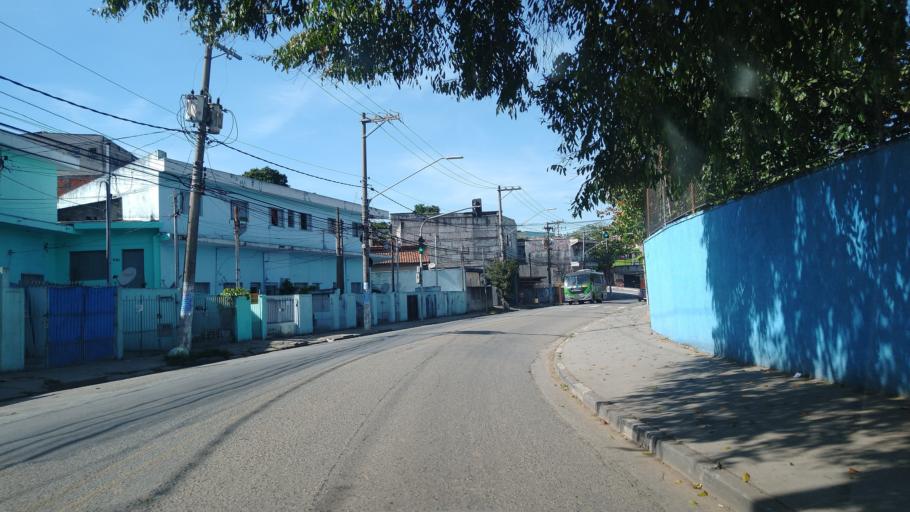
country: BR
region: Sao Paulo
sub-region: Sao Paulo
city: Sao Paulo
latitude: -23.4638
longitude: -46.6686
